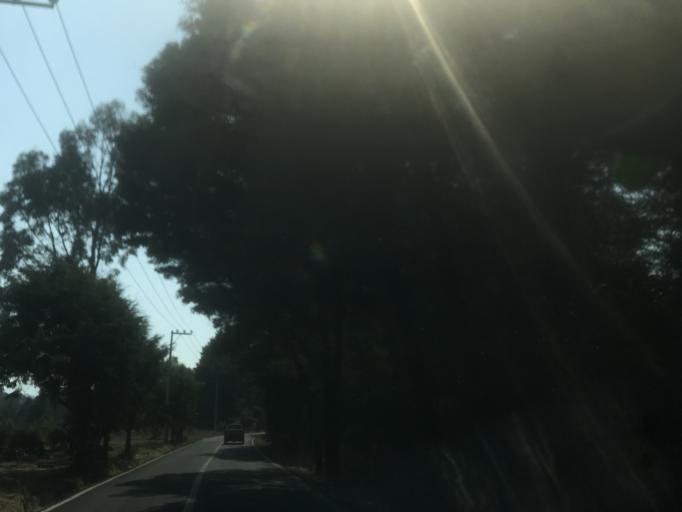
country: MX
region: Mexico
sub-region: Atlautla
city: San Juan Tepecoculco
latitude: 18.9970
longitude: -98.7812
